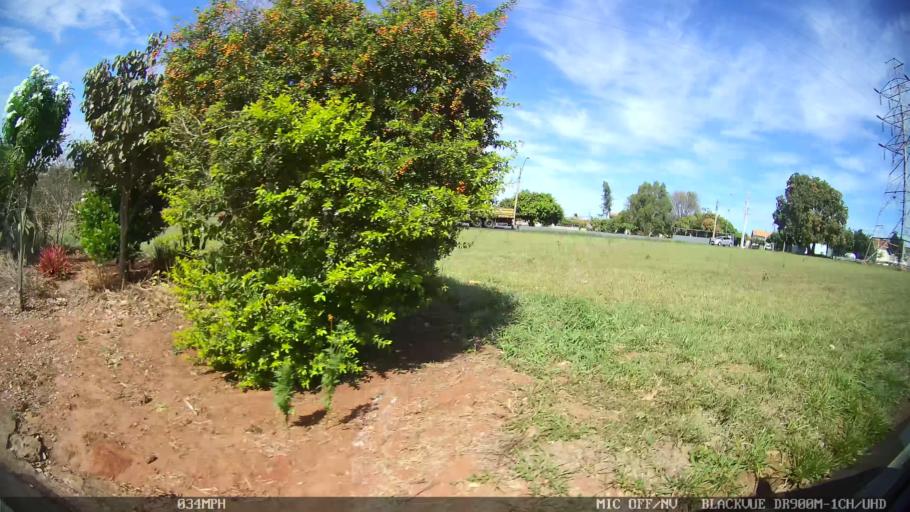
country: BR
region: Sao Paulo
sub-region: Sao Jose Do Rio Preto
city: Sao Jose do Rio Preto
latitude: -20.8441
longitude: -49.3641
